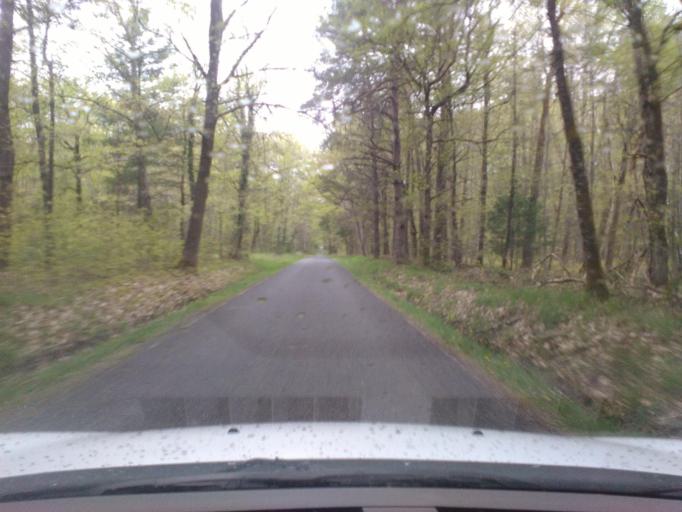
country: FR
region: Rhone-Alpes
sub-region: Departement de l'Ain
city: Saint-Etienne-du-Bois
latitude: 46.2533
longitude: 5.2873
